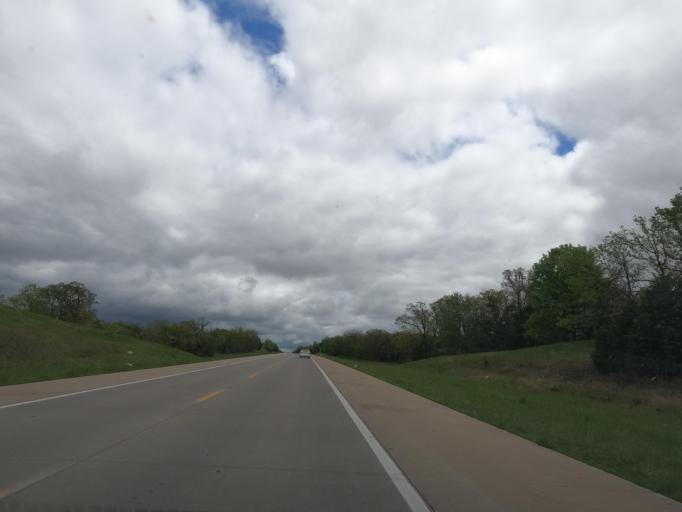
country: US
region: Kansas
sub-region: Wilson County
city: Neodesha
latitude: 37.3552
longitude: -95.6669
